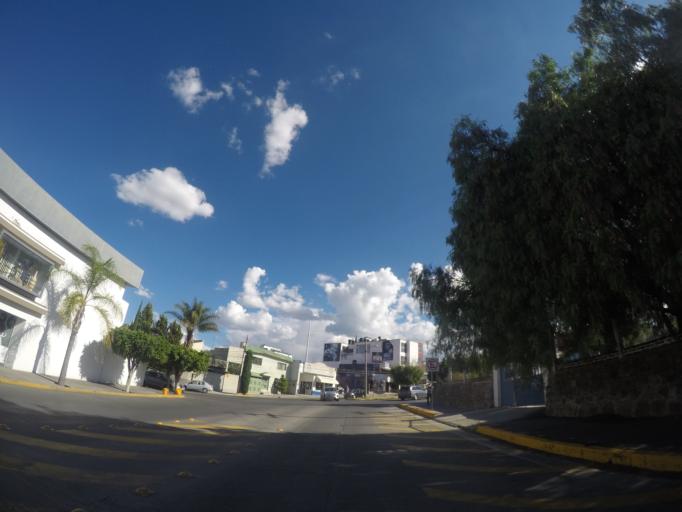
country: MX
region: San Luis Potosi
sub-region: San Luis Potosi
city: San Luis Potosi
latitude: 22.1460
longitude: -101.0187
